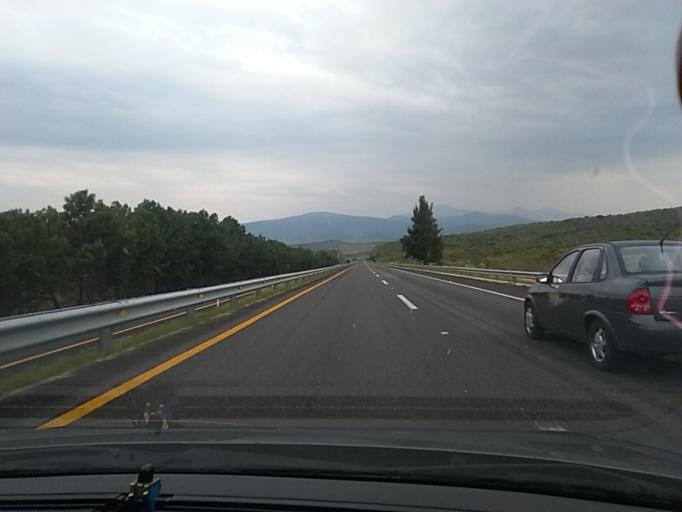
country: MX
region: Michoacan
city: Penjamillo de Degollado
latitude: 20.0698
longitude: -101.9668
